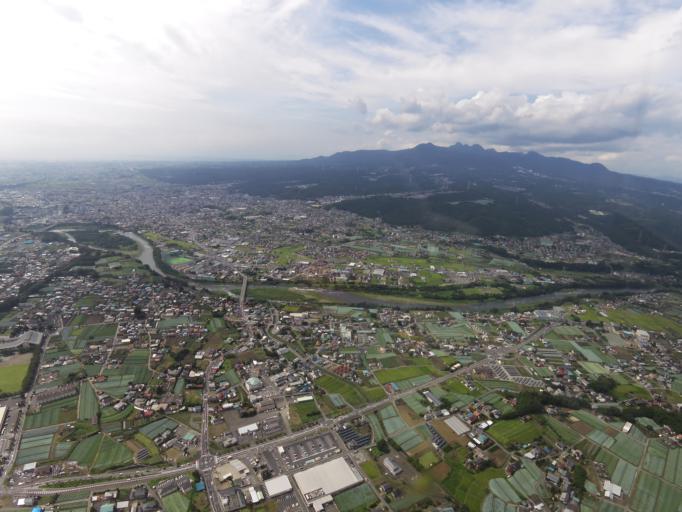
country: JP
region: Gunma
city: Shibukawa
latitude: 36.5241
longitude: 139.0124
